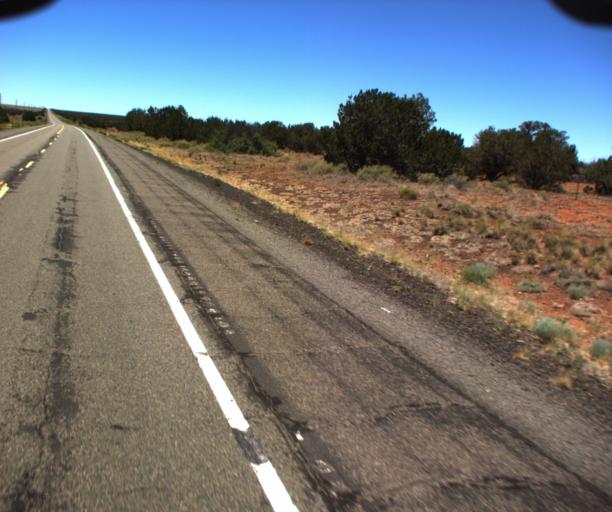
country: US
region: Arizona
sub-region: Coconino County
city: LeChee
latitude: 34.8276
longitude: -110.9549
